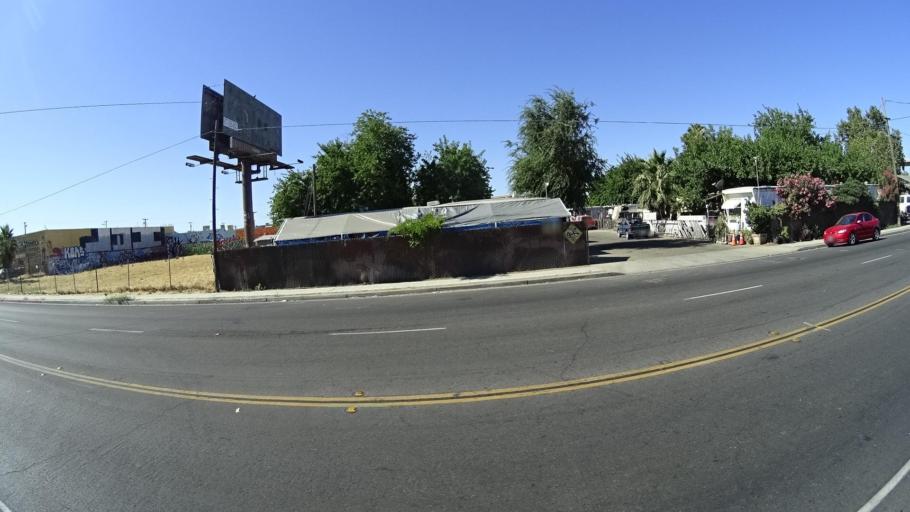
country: US
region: California
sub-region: Fresno County
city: Fresno
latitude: 36.7578
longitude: -119.7469
